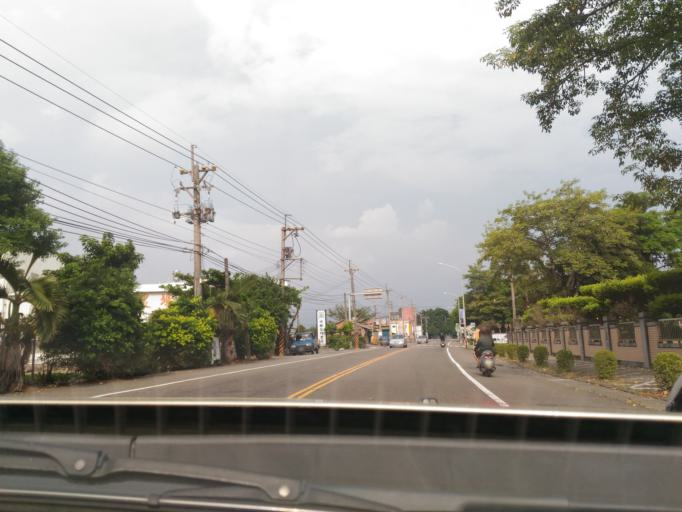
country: TW
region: Taiwan
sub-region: Chiayi
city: Taibao
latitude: 23.6033
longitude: 120.2421
